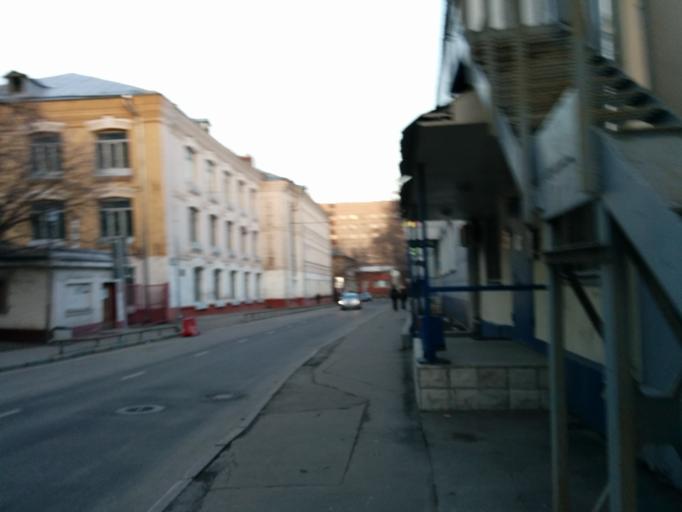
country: RU
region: Moscow
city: Novyye Cheremushki
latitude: 55.7188
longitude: 37.6017
